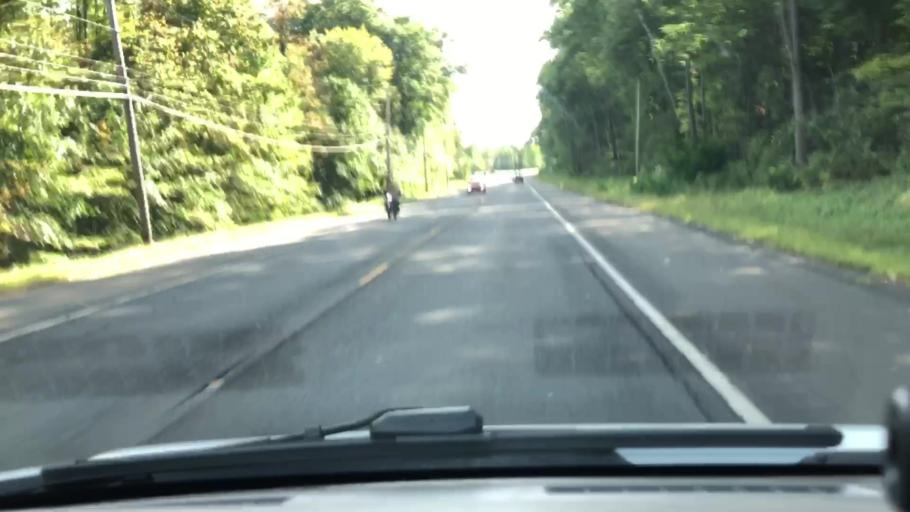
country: US
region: Massachusetts
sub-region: Hampshire County
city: Easthampton
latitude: 42.2960
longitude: -72.6574
